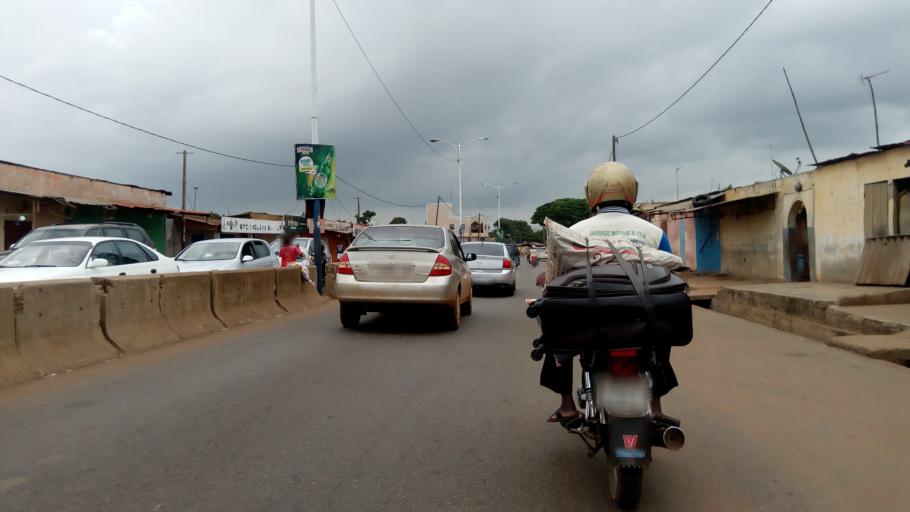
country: TG
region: Maritime
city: Lome
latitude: 6.2220
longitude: 1.2092
